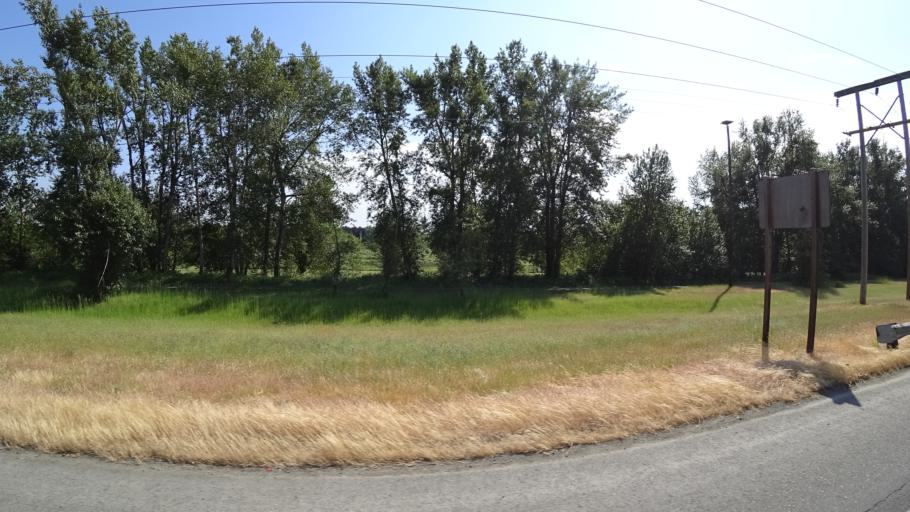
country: US
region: Oregon
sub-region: Multnomah County
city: Fairview
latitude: 45.5588
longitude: -122.4430
